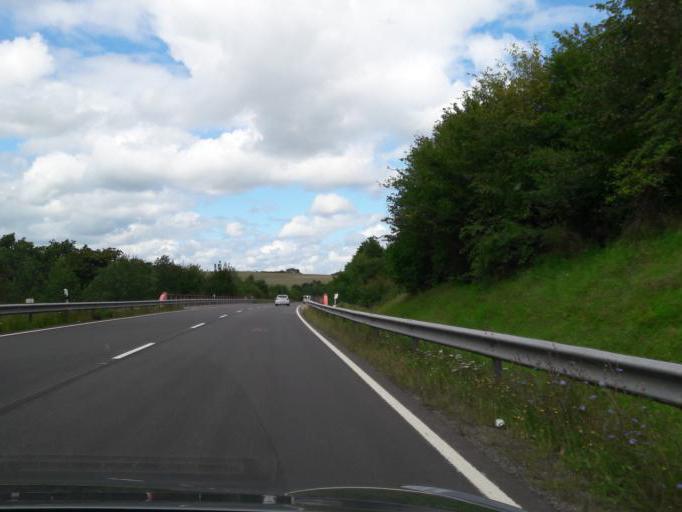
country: DE
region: Rheinland-Pfalz
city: Mettweiler
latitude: 49.6038
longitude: 7.3061
